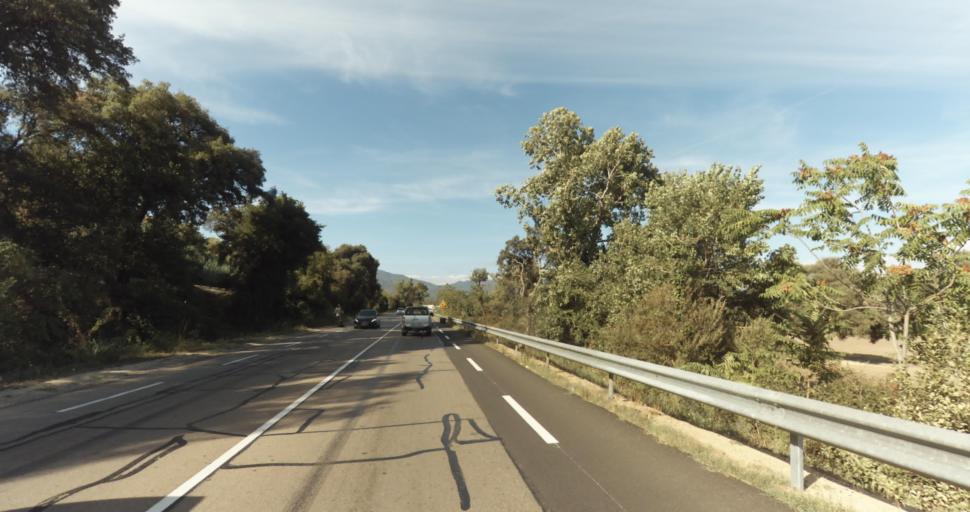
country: FR
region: Corsica
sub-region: Departement de la Corse-du-Sud
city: Afa
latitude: 41.9451
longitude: 8.8113
